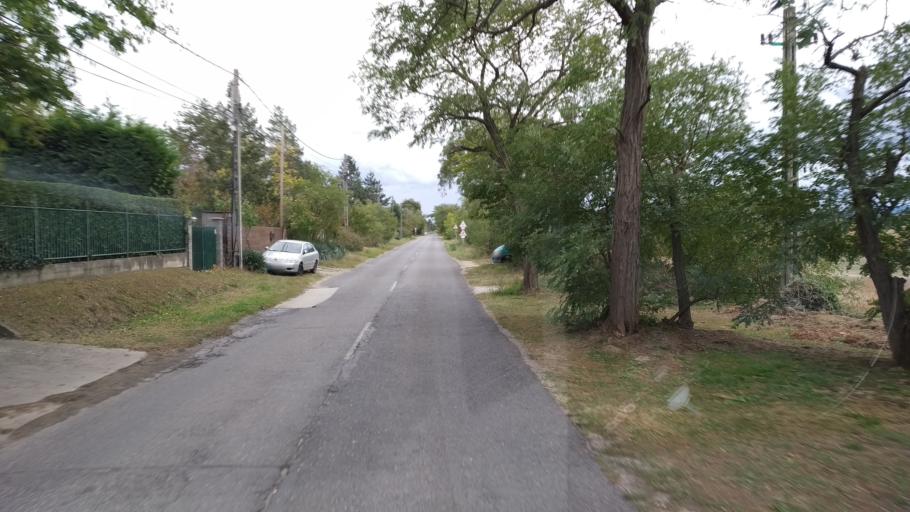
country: HU
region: Pest
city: Leanyfalu
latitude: 47.7104
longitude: 19.1064
